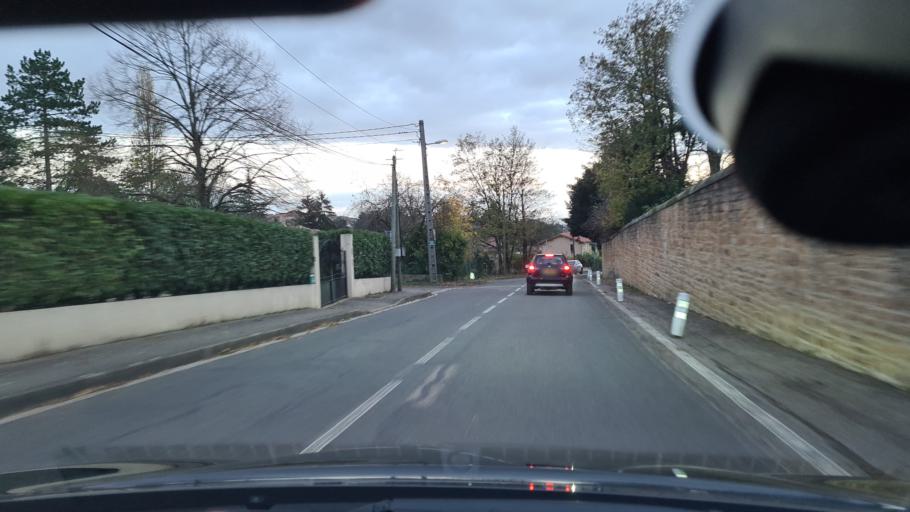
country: FR
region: Rhone-Alpes
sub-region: Departement du Rhone
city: Fontaines-sur-Saone
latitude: 45.8238
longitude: 4.8103
